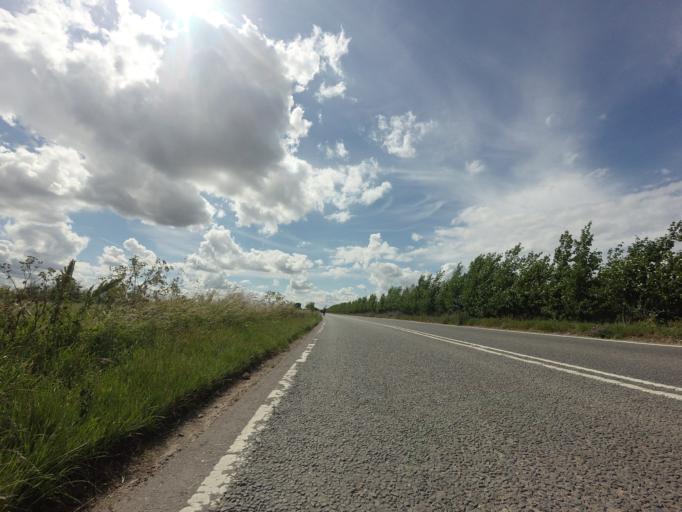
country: GB
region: England
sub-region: Medway
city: Stoke
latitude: 51.4488
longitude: 0.6104
